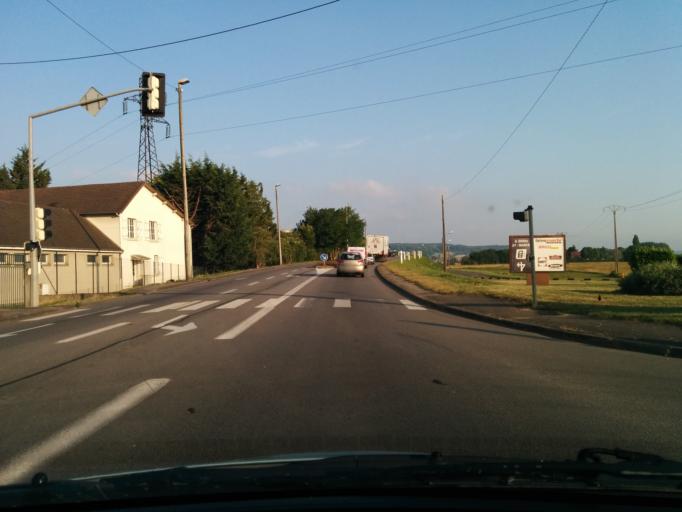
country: FR
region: Haute-Normandie
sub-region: Departement de l'Eure
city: Vernon
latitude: 49.1040
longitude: 1.4625
